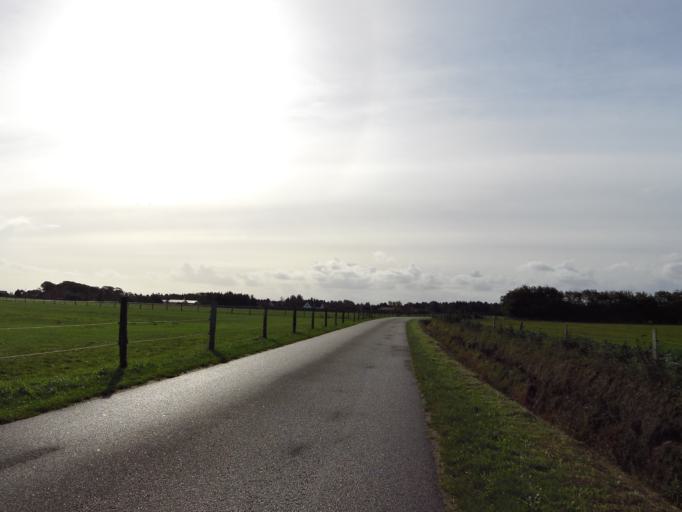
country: DK
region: South Denmark
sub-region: Varde Kommune
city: Oksbol
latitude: 55.5547
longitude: 8.2230
